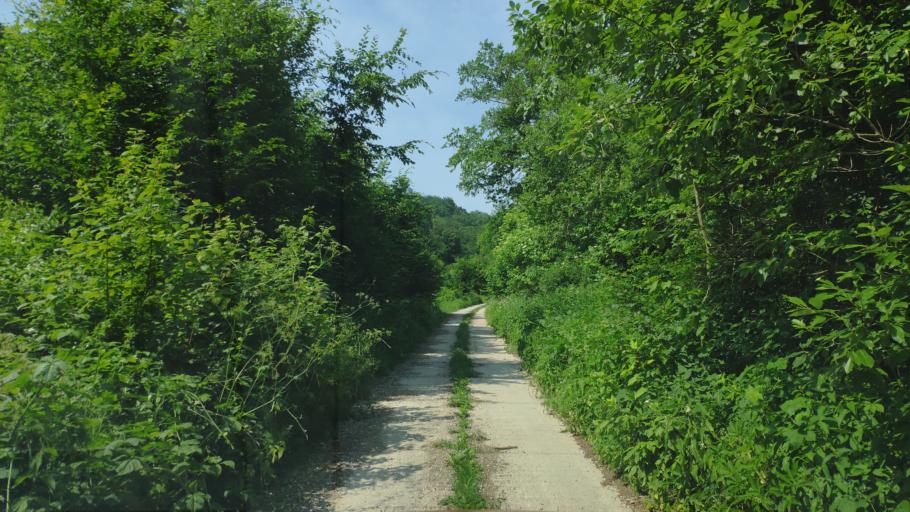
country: SK
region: Presovsky
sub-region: Okres Presov
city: Presov
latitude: 48.9684
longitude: 21.1448
